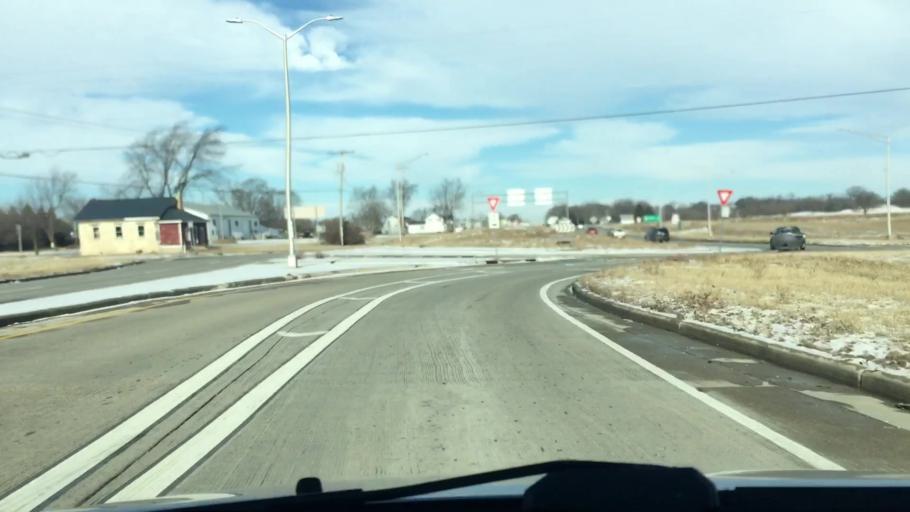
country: US
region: Wisconsin
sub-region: Waukesha County
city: Mukwonago
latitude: 42.9220
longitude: -88.3458
